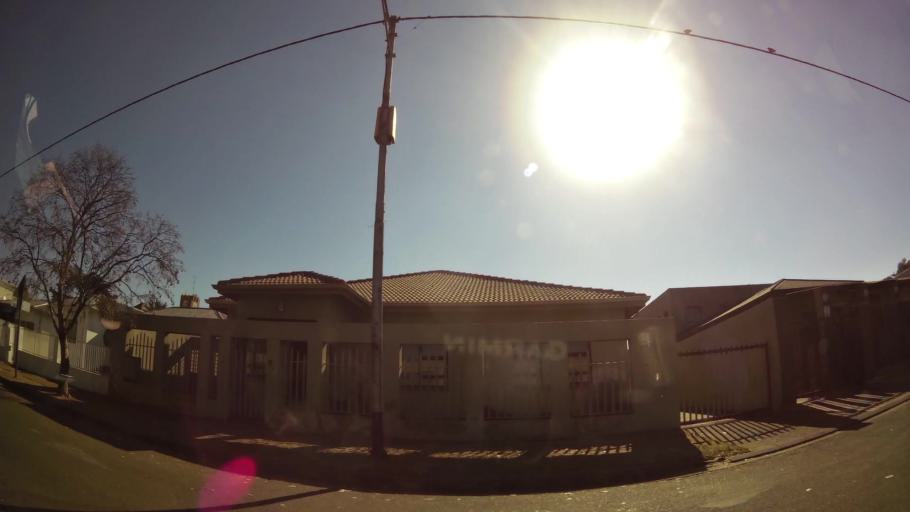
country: ZA
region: Gauteng
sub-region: City of Johannesburg Metropolitan Municipality
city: Johannesburg
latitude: -26.1917
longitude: 27.9860
